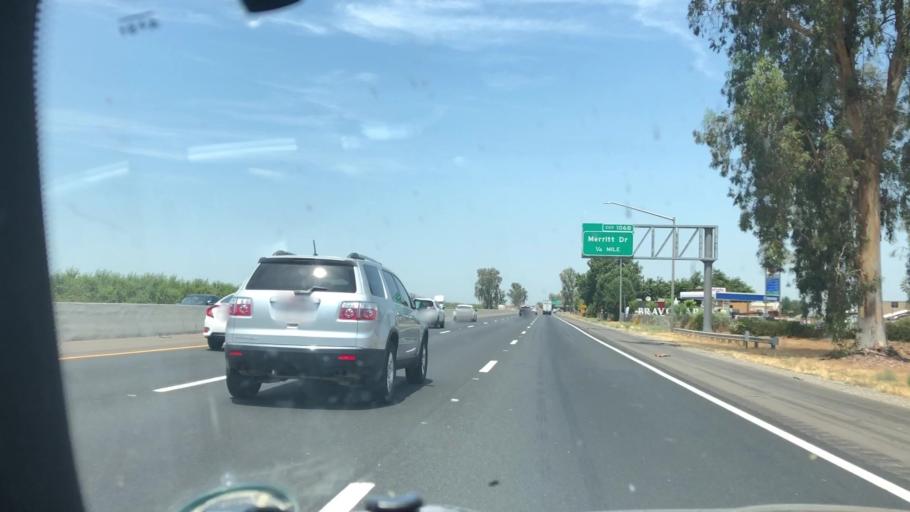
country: US
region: California
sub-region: Tulare County
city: London
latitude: 36.4464
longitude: -119.4849
